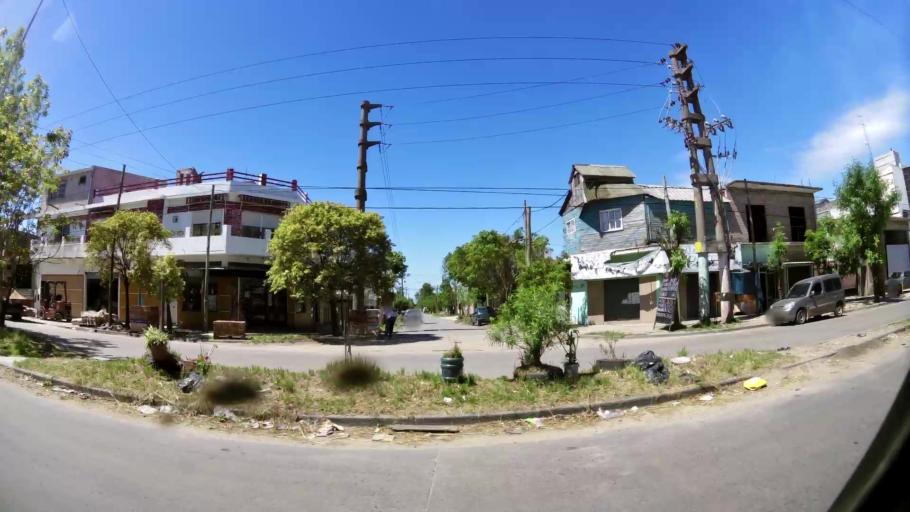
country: AR
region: Buenos Aires
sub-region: Partido de Almirante Brown
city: Adrogue
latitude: -34.7496
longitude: -58.3400
